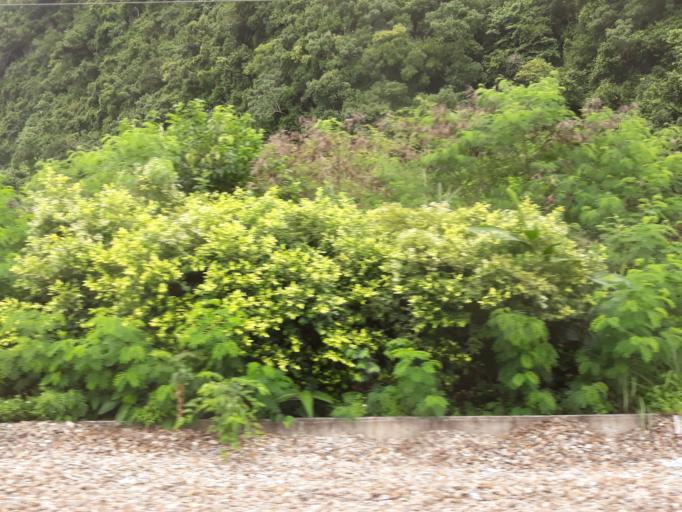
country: TW
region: Taiwan
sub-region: Yilan
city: Yilan
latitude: 24.4460
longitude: 121.7768
